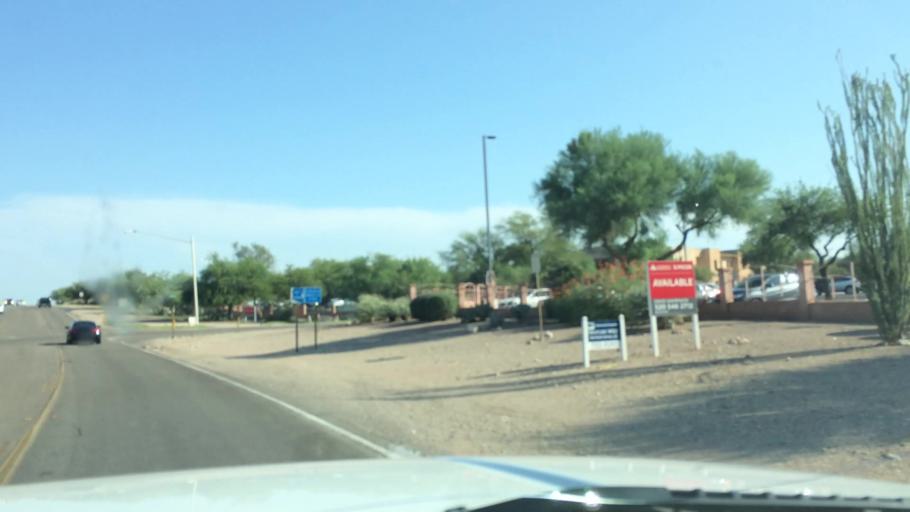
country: US
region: Arizona
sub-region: Pima County
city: Catalina Foothills
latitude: 32.3071
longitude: -110.8442
